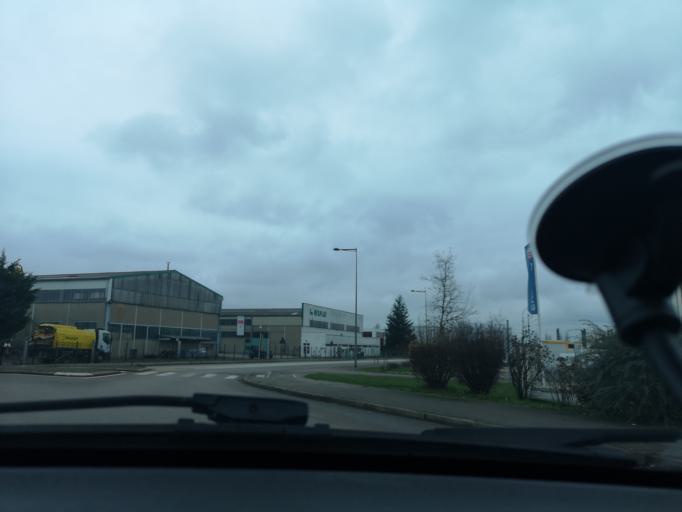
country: FR
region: Bourgogne
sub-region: Departement de Saone-et-Loire
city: Virey-le-Grand
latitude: 46.8240
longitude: 4.8640
